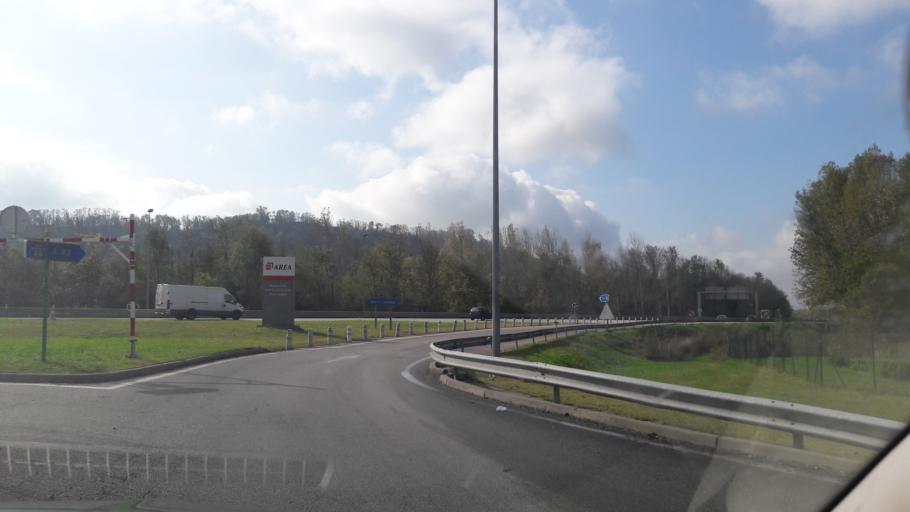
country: FR
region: Rhone-Alpes
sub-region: Departement de la Savoie
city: Coise-Saint-Jean-Pied-Gauthier
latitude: 45.5478
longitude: 6.1528
